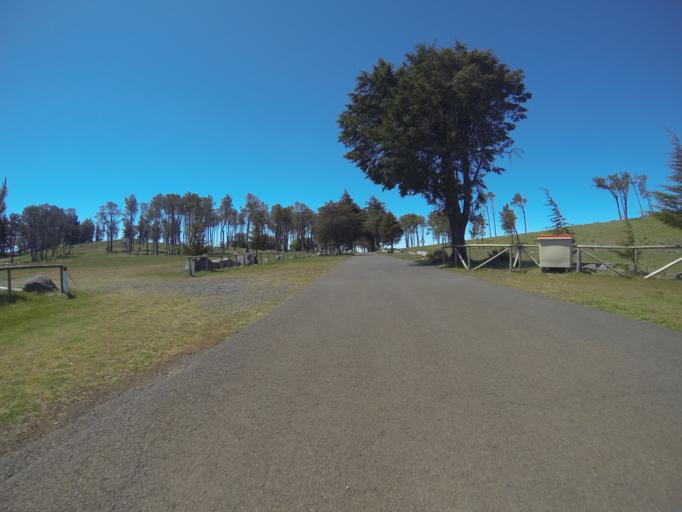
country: PT
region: Madeira
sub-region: Funchal
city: Nossa Senhora do Monte
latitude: 32.7119
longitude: -16.9117
